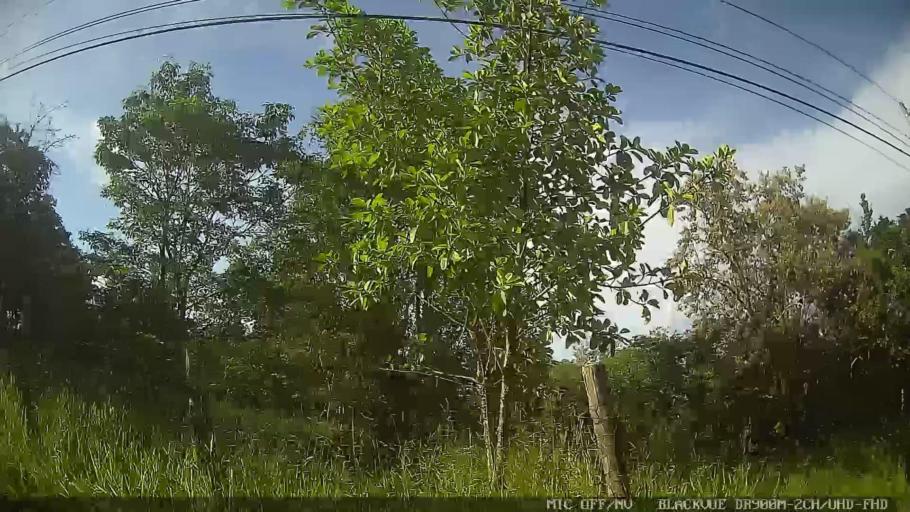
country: BR
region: Sao Paulo
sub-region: Tiete
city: Tiete
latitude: -23.0858
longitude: -47.6910
